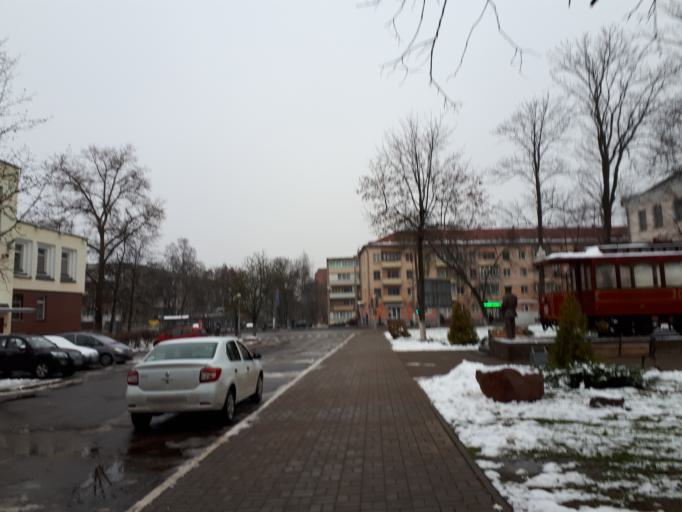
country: BY
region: Vitebsk
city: Vitebsk
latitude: 55.1924
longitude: 30.2211
